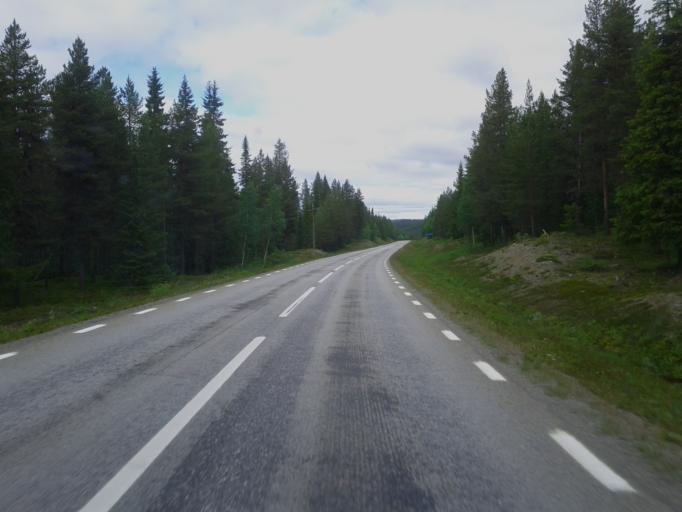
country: SE
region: Vaesterbotten
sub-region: Storumans Kommun
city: Fristad
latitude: 65.3687
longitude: 16.5194
